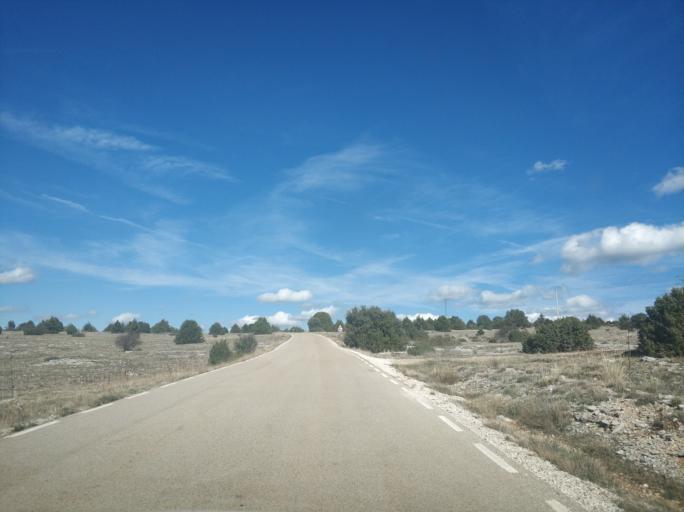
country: ES
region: Castille and Leon
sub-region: Provincia de Soria
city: Espejon
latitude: 41.8366
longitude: -3.2465
